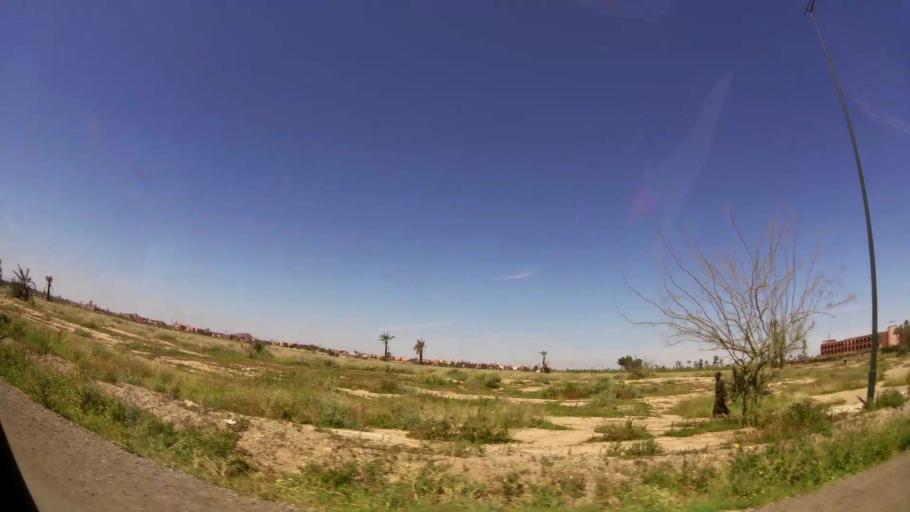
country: MA
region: Marrakech-Tensift-Al Haouz
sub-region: Marrakech
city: Marrakesh
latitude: 31.6808
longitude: -7.9914
